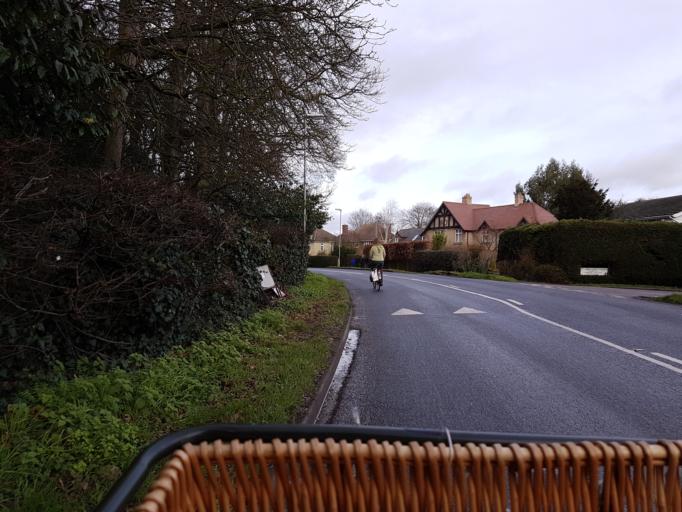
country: GB
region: England
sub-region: Cambridgeshire
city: Girton
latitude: 52.2272
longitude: 0.0877
